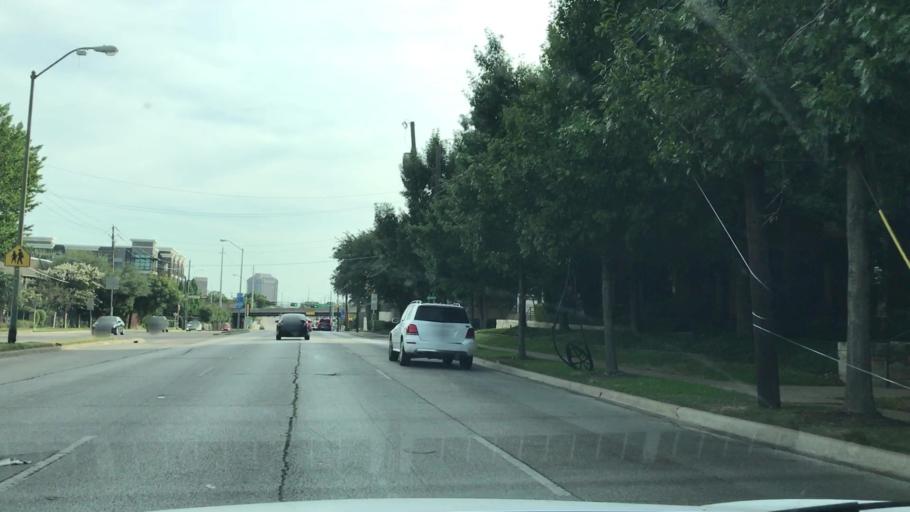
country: US
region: Texas
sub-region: Dallas County
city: Dallas
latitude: 32.8129
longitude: -96.8161
